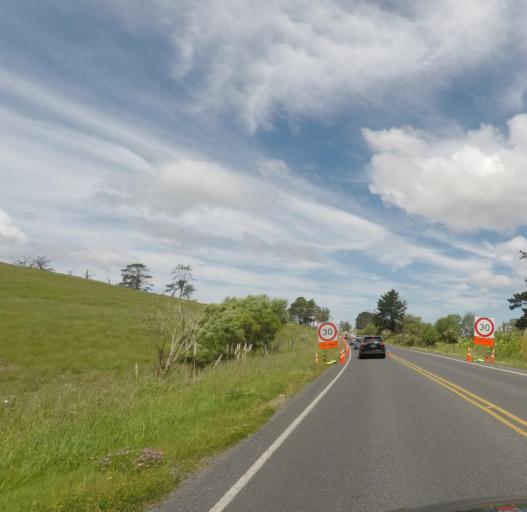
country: NZ
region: Auckland
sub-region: Auckland
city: Rothesay Bay
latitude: -36.6680
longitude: 174.6800
